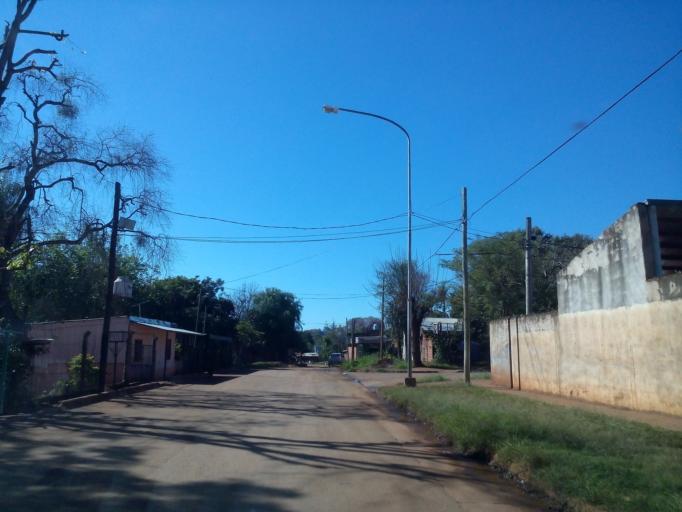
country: AR
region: Misiones
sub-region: Departamento de Capital
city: Posadas
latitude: -27.3897
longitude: -55.9448
